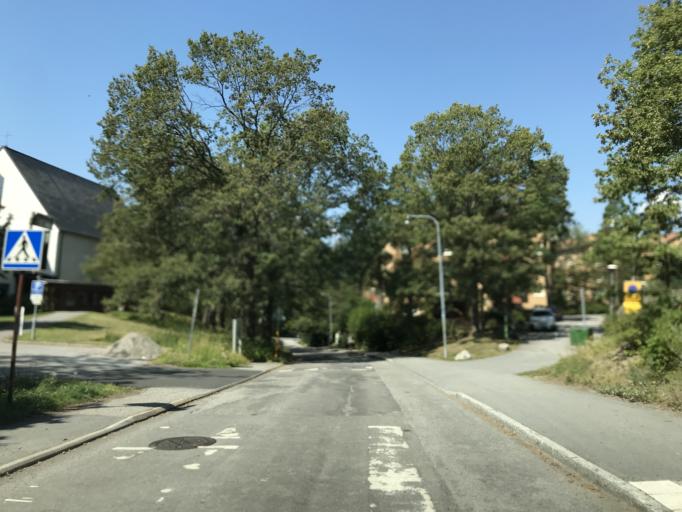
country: SE
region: Stockholm
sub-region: Stockholms Kommun
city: Bromma
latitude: 59.3346
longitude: 17.9544
